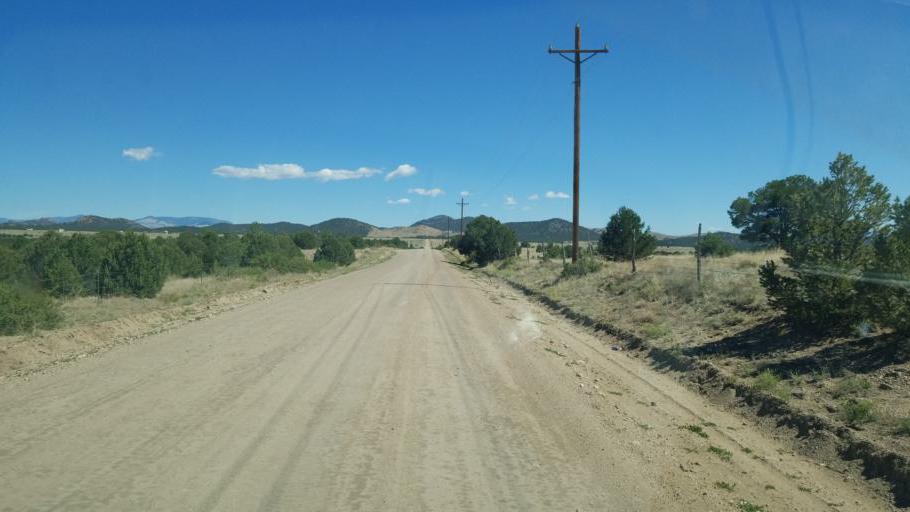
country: US
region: Colorado
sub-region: Custer County
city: Westcliffe
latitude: 38.2667
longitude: -105.5011
